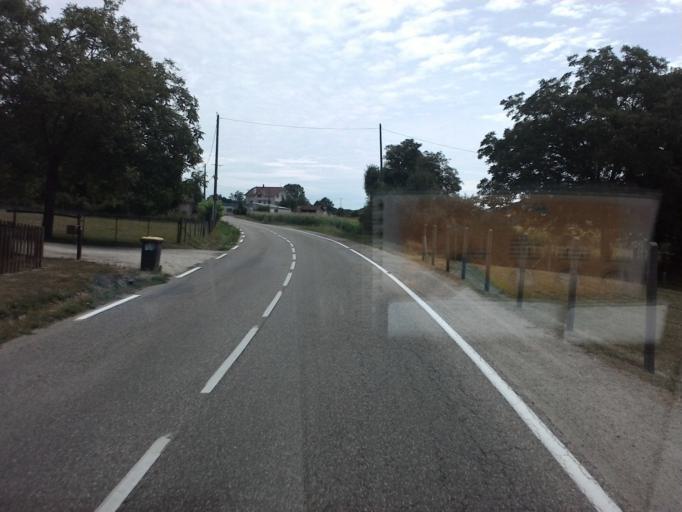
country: FR
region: Rhone-Alpes
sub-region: Departement de l'Isere
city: Montferrat
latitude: 45.4788
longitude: 5.5629
